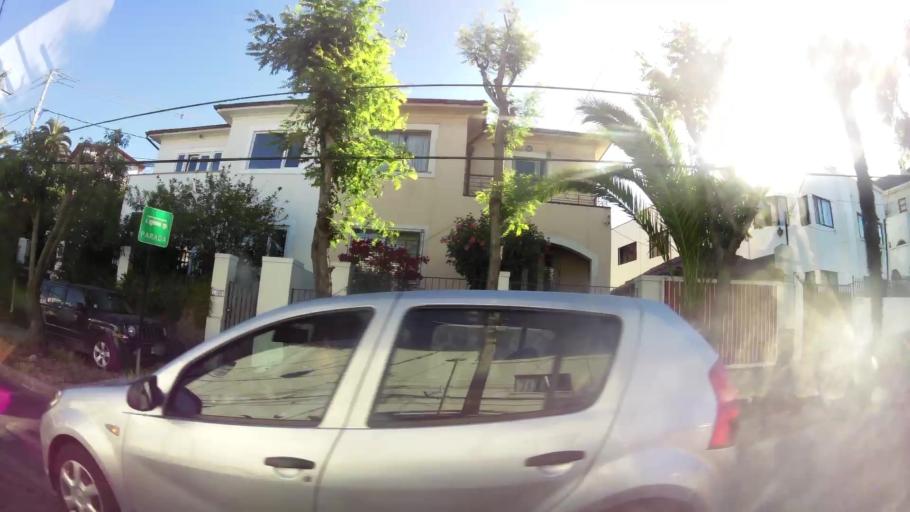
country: CL
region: Valparaiso
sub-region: Provincia de Valparaiso
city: Vina del Mar
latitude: -33.0299
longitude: -71.5772
